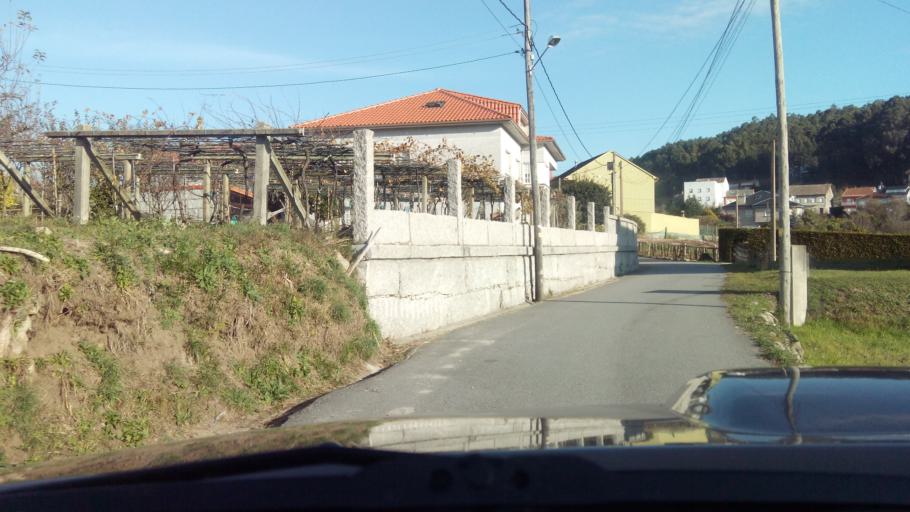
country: ES
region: Galicia
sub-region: Provincia de Pontevedra
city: Marin
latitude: 42.3628
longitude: -8.7034
